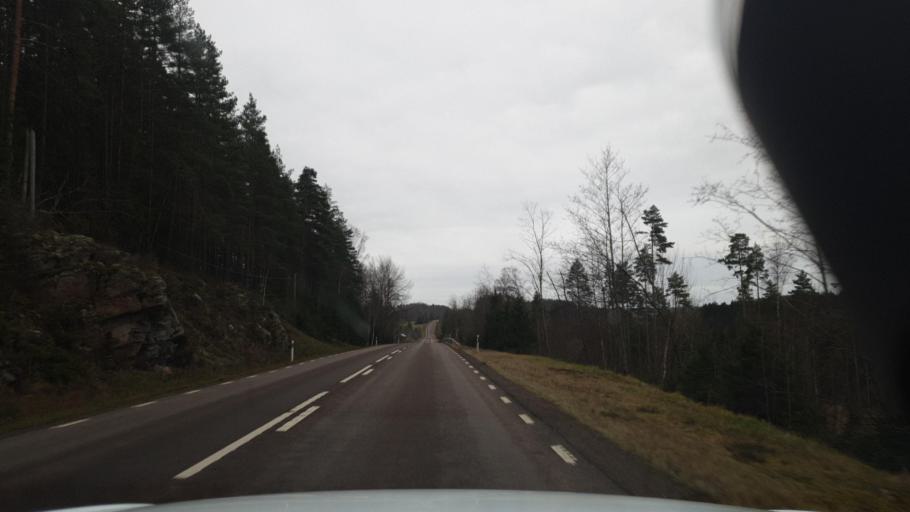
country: SE
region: Vaermland
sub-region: Karlstads Kommun
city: Edsvalla
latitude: 59.5855
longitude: 13.0141
